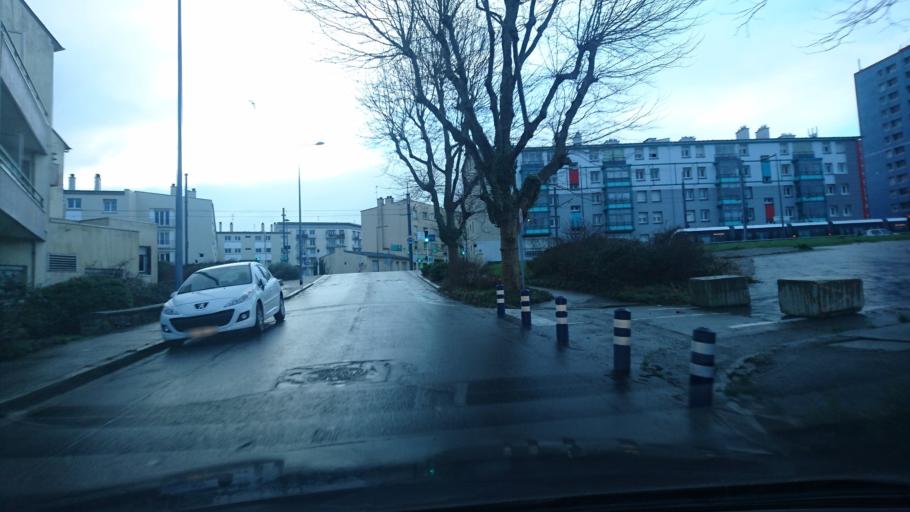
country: FR
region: Brittany
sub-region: Departement du Finistere
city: Brest
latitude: 48.3901
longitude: -4.5041
